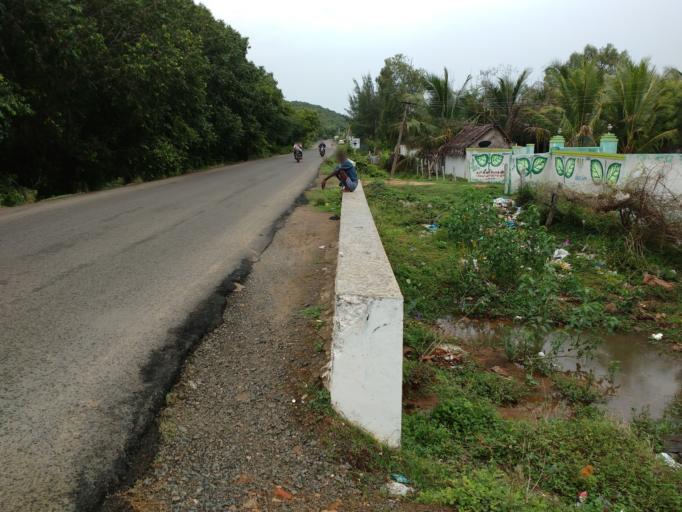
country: IN
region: Tamil Nadu
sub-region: Kancheepuram
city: Nandambakkam
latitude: 12.9516
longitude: 80.0617
